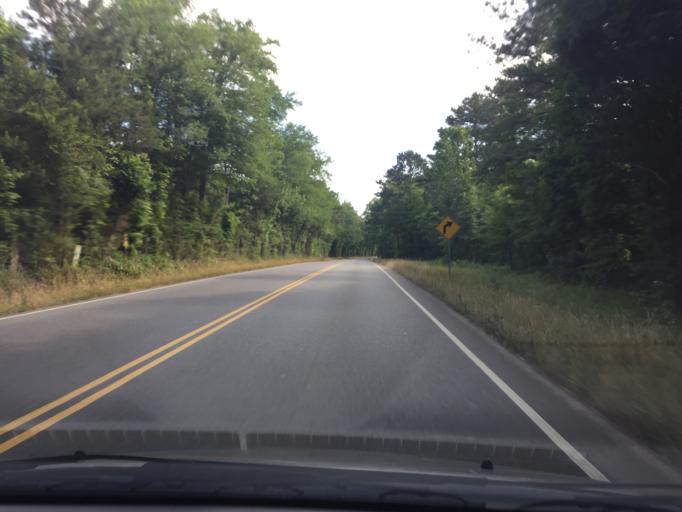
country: US
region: Tennessee
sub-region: Hamilton County
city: Collegedale
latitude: 35.1038
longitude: -85.0050
